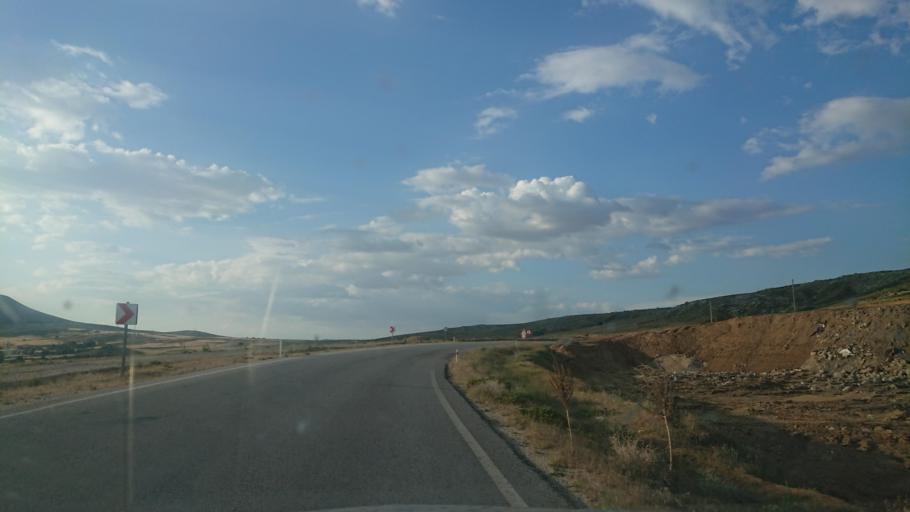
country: TR
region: Aksaray
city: Balci
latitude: 38.5967
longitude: 34.1014
